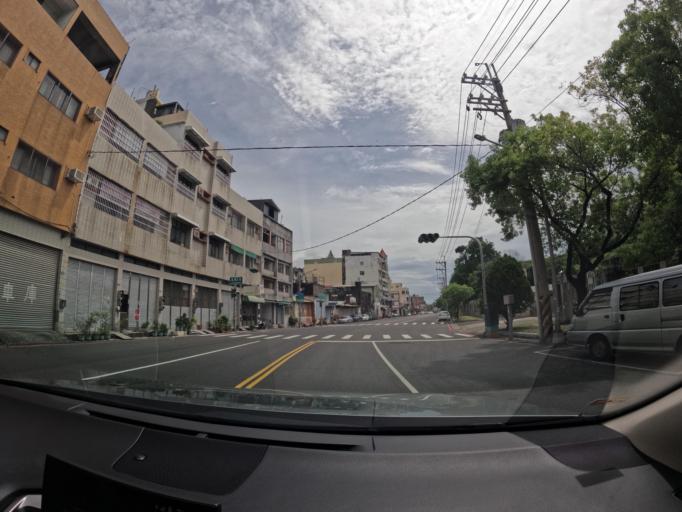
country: TW
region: Kaohsiung
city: Kaohsiung
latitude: 22.6879
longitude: 120.2911
